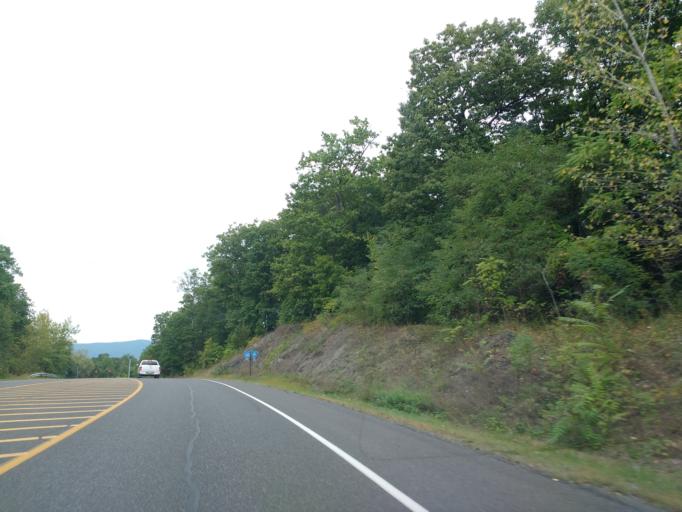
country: US
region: New York
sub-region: Ulster County
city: Lincoln Park
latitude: 41.9584
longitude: -73.9814
